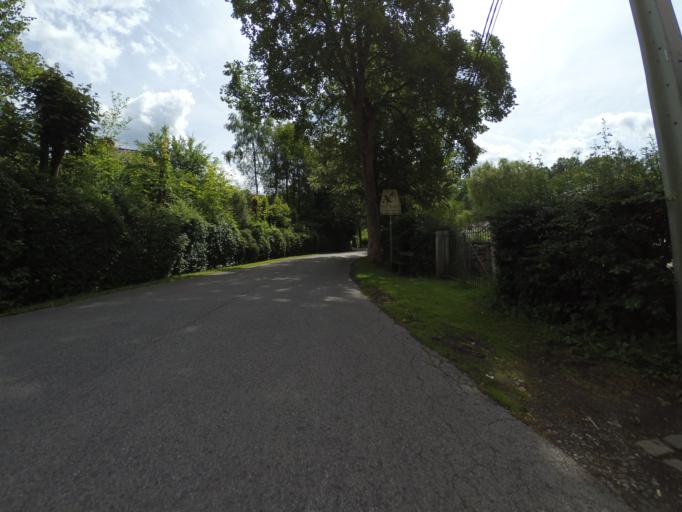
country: BE
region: Wallonia
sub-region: Province de Liege
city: Eupen
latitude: 50.6195
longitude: 6.0570
